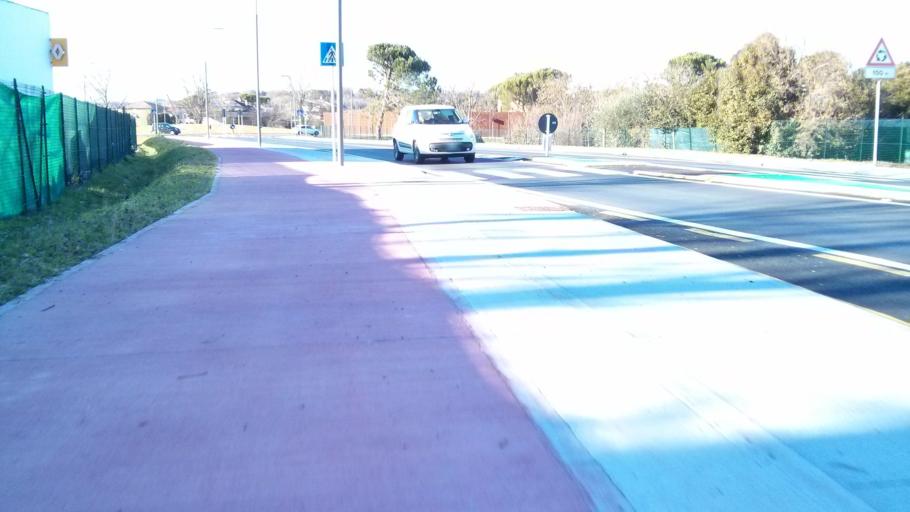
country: IT
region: The Marches
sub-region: Provincia di Pesaro e Urbino
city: Centinarola
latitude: 43.8387
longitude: 13.0018
